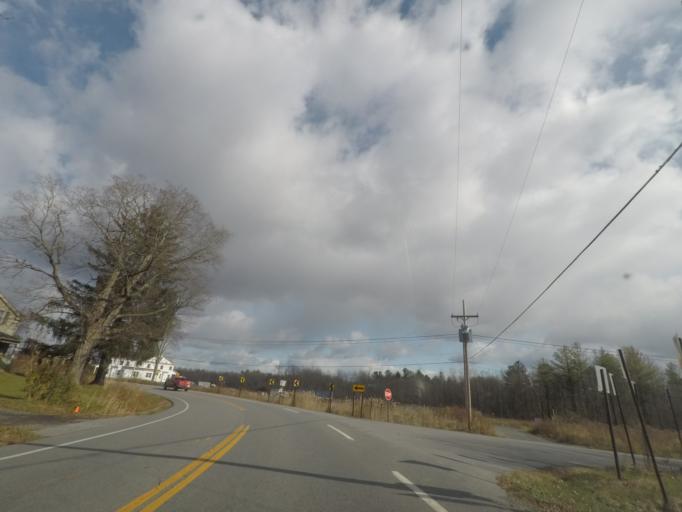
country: US
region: New York
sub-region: Saratoga County
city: Country Knolls
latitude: 42.9274
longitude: -73.8376
